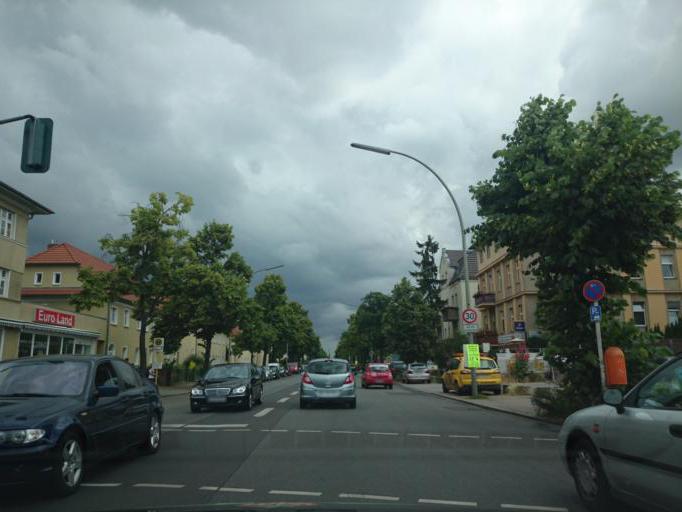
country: DE
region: Berlin
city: Marienfelde
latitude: 52.4176
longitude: 13.3667
